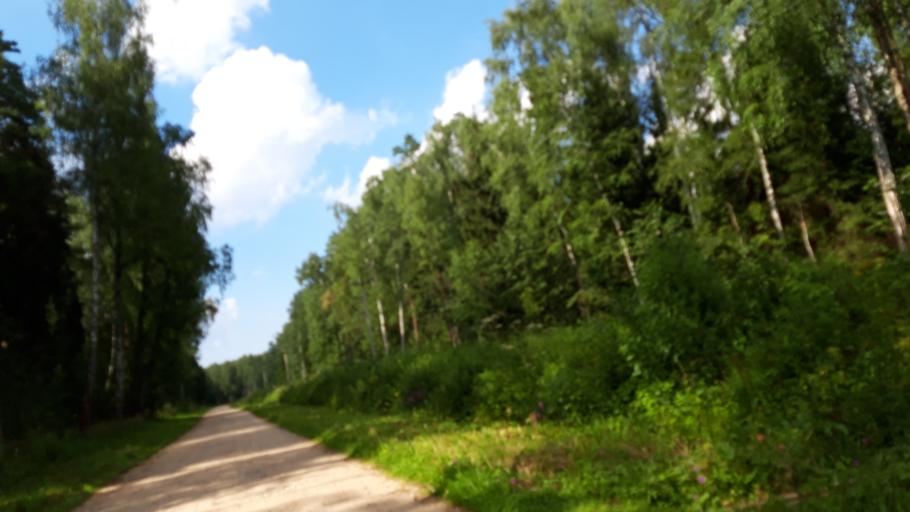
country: RU
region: Tverskaya
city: Konakovo
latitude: 56.6853
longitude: 36.7113
